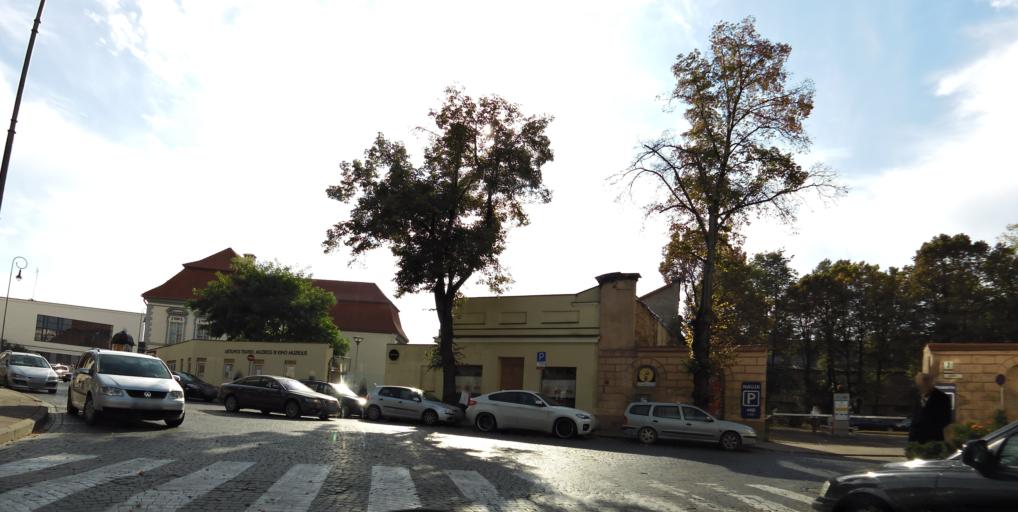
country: LT
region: Vilnius County
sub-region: Vilnius
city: Vilnius
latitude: 54.6819
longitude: 25.2801
